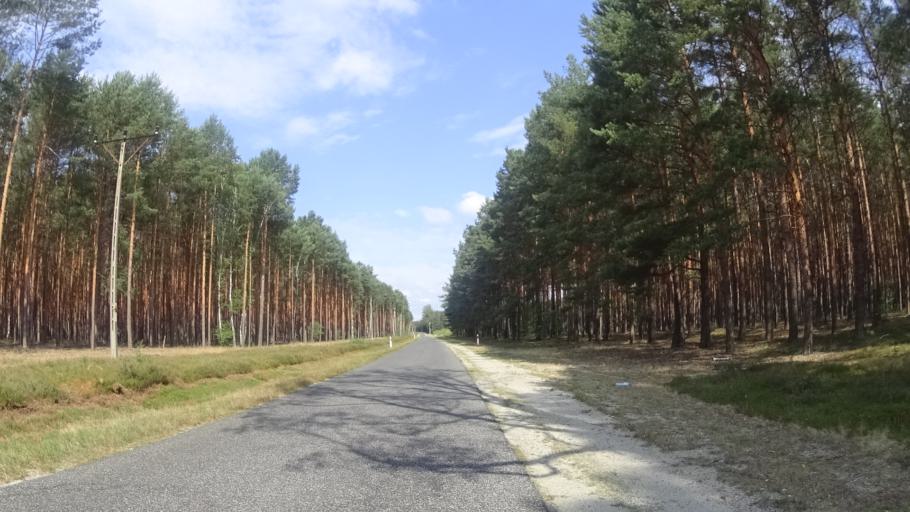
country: PL
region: Lubusz
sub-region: Powiat zarski
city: Leknica
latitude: 51.5149
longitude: 14.8318
